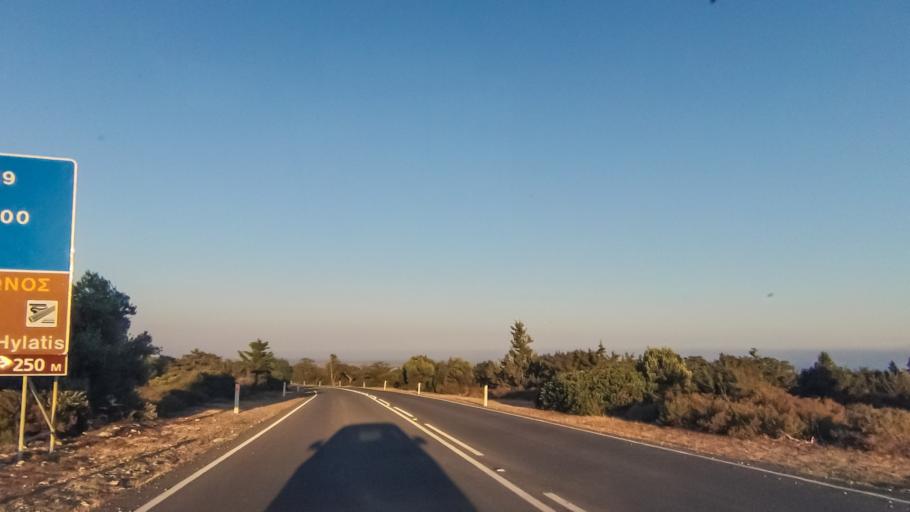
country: CY
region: Limassol
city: Sotira
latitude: 34.6704
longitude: 32.8608
